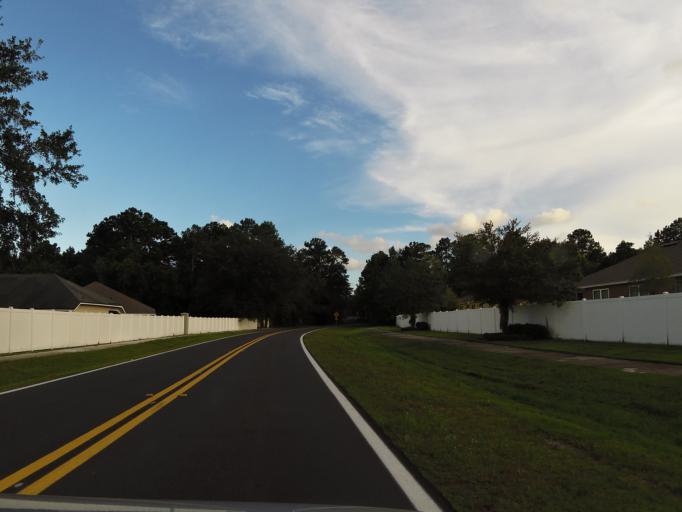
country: US
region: Florida
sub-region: Duval County
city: Jacksonville
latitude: 30.4339
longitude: -81.6931
